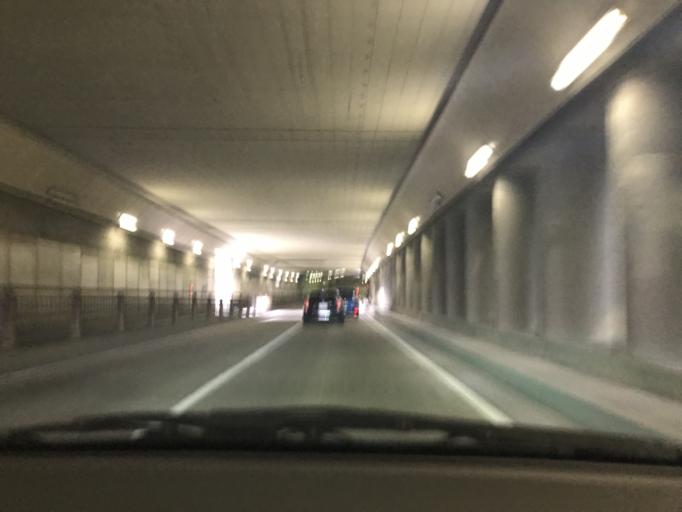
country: JP
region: Kanagawa
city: Fujisawa
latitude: 35.3520
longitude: 139.4447
